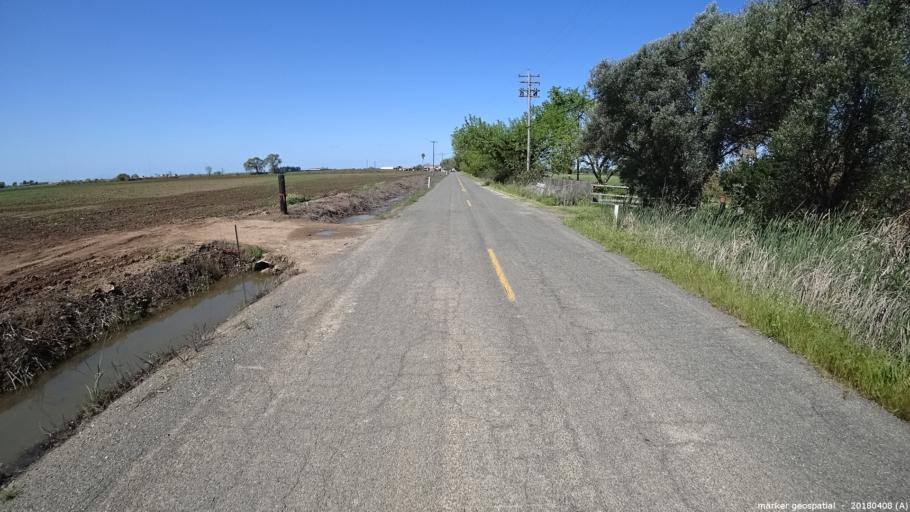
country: US
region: California
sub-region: Sacramento County
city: Laguna
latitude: 38.3358
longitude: -121.4233
